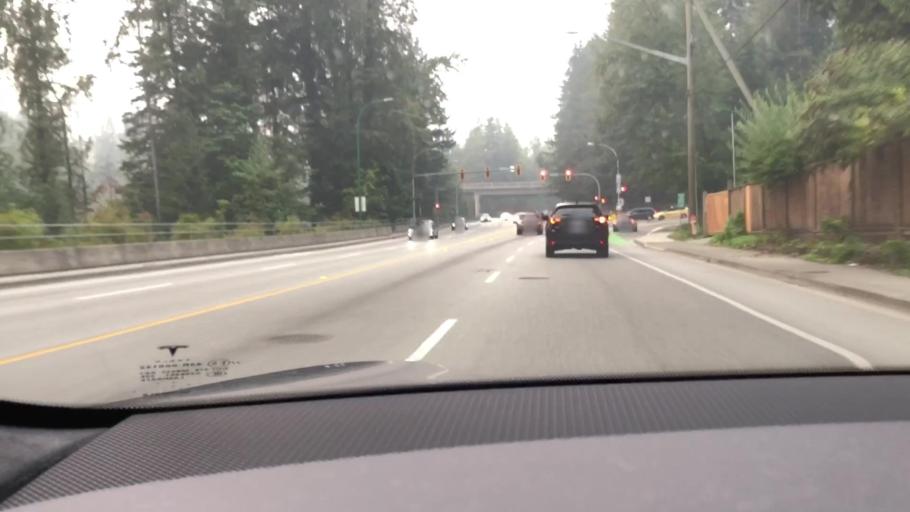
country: CA
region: British Columbia
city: West End
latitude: 49.3305
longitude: -123.1172
